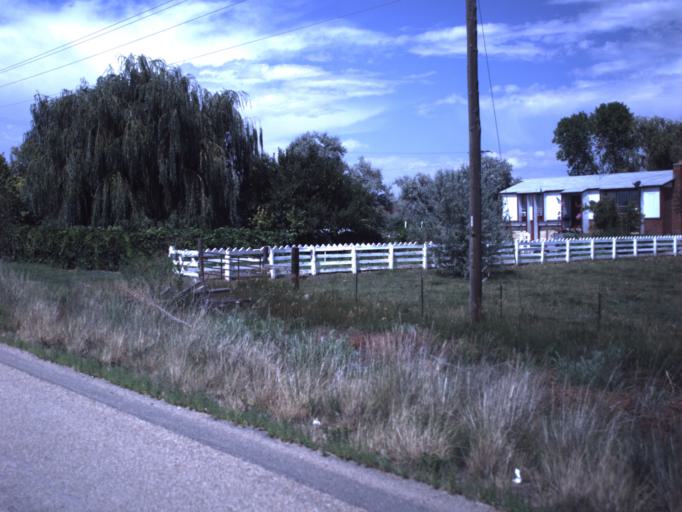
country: US
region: Utah
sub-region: Duchesne County
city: Roosevelt
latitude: 40.3020
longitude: -109.8775
